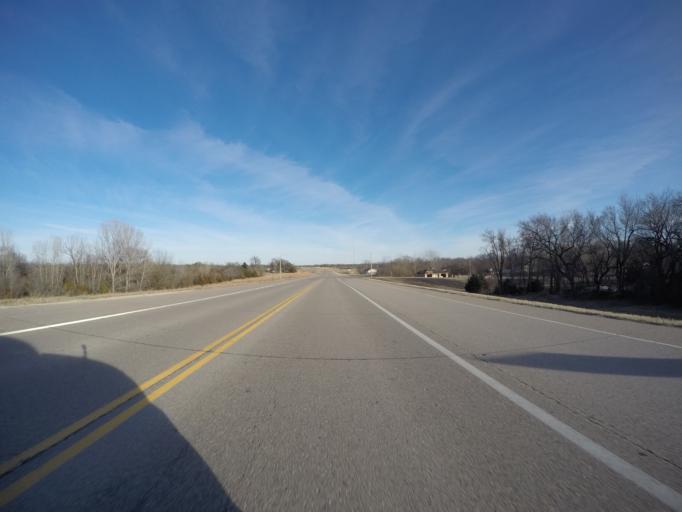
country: US
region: Kansas
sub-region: Marion County
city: Peabody
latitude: 38.1757
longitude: -97.1049
